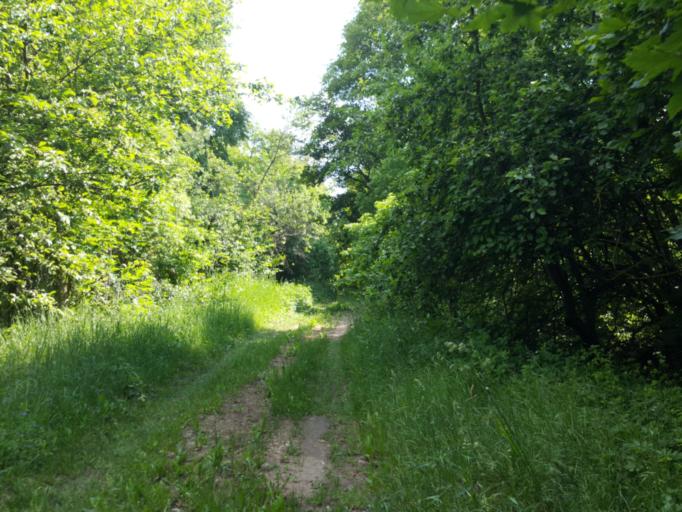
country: BY
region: Brest
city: Vysokaye
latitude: 52.4546
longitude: 23.5849
